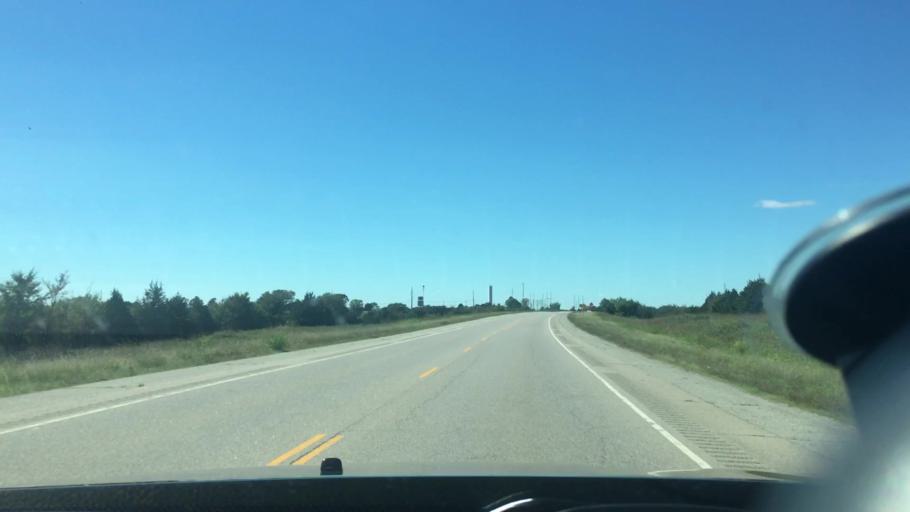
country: US
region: Oklahoma
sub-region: Coal County
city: Coalgate
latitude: 34.6112
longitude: -96.4291
